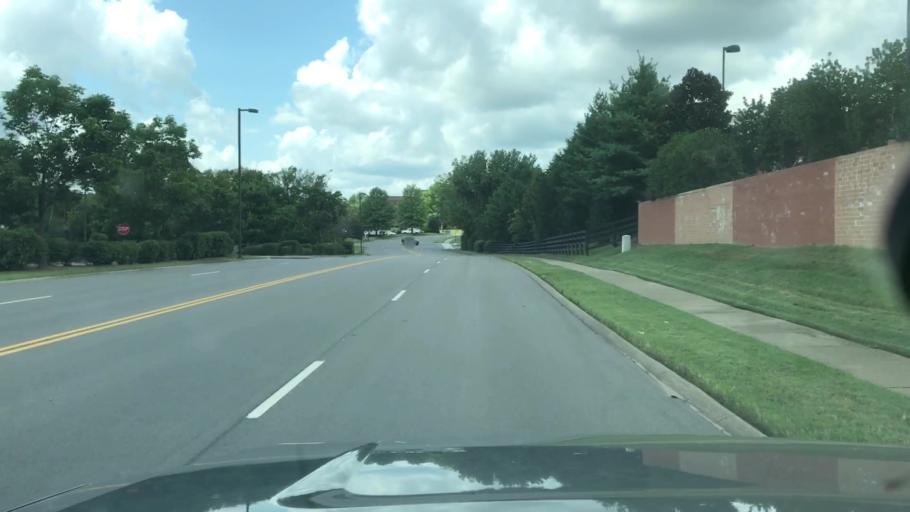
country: US
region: Tennessee
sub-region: Williamson County
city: Brentwood
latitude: 36.0363
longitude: -86.7990
